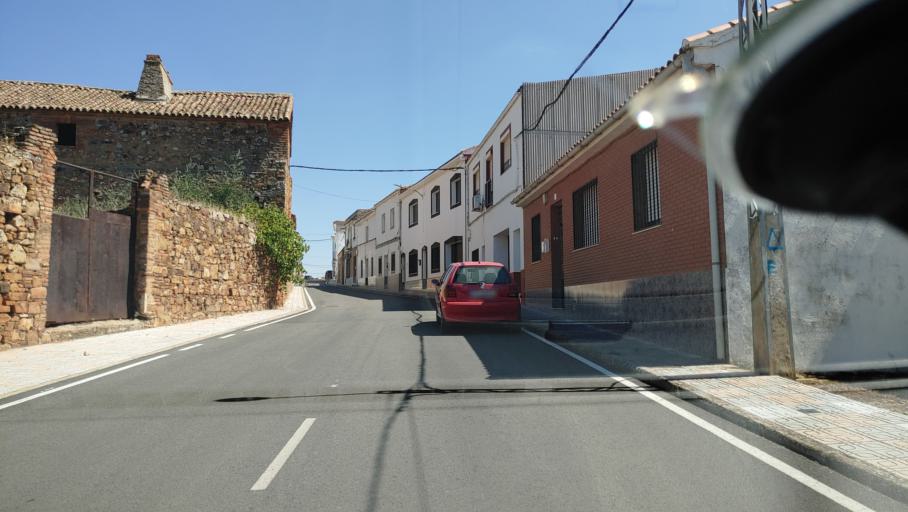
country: ES
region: Castille-La Mancha
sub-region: Provincia de Ciudad Real
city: Alamillo
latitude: 38.7377
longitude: -4.7129
